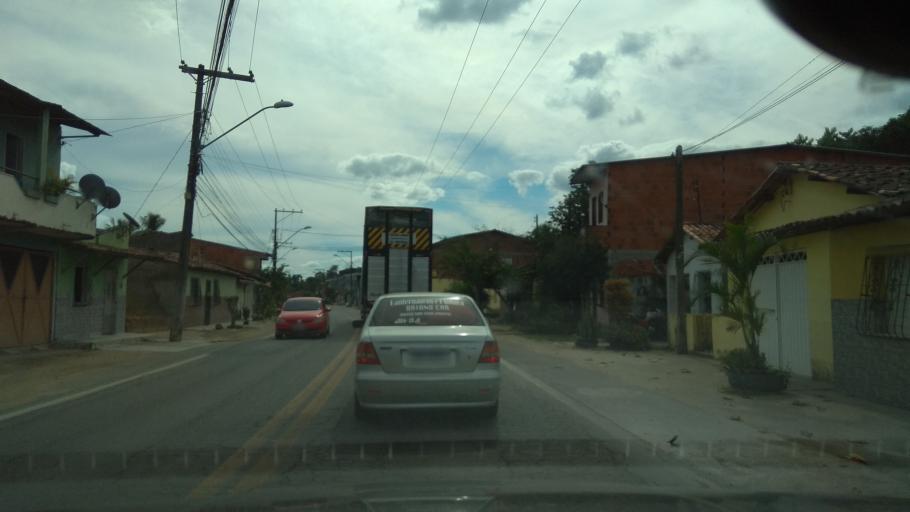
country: BR
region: Bahia
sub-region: Ipiau
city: Ipiau
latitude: -14.1264
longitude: -39.7579
